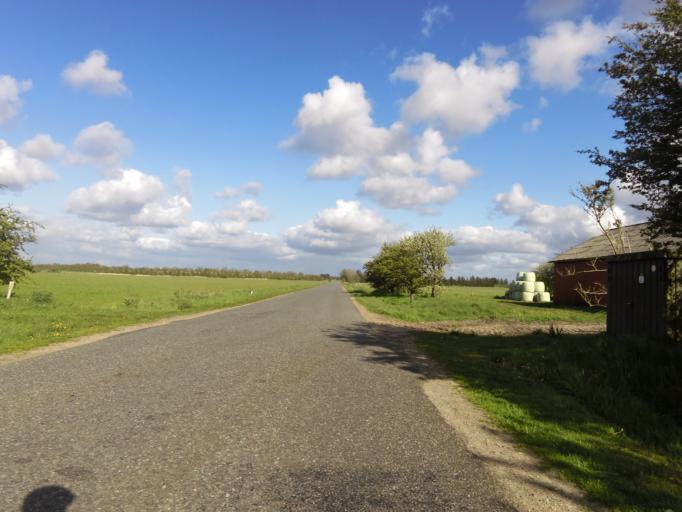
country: DK
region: South Denmark
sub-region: Esbjerg Kommune
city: Ribe
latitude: 55.2601
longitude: 8.7789
